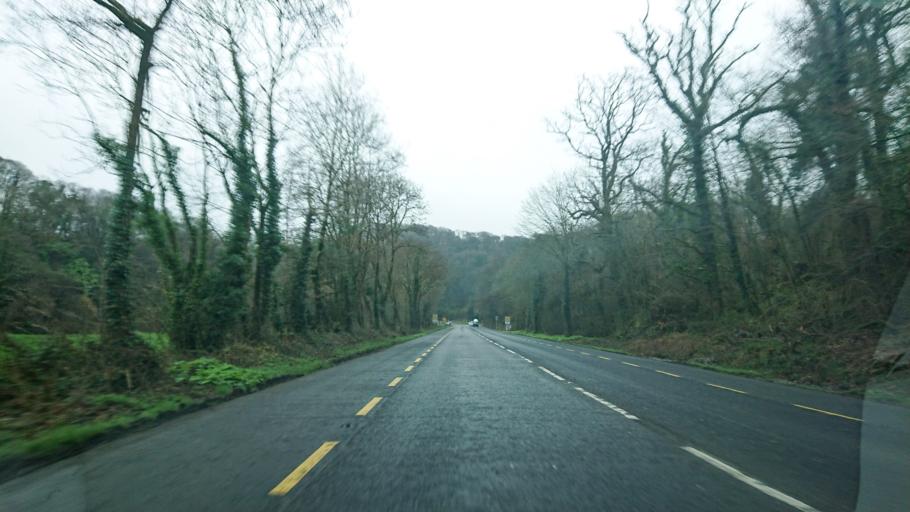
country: IE
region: Munster
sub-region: County Cork
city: Bandon
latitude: 51.7671
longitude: -8.6859
